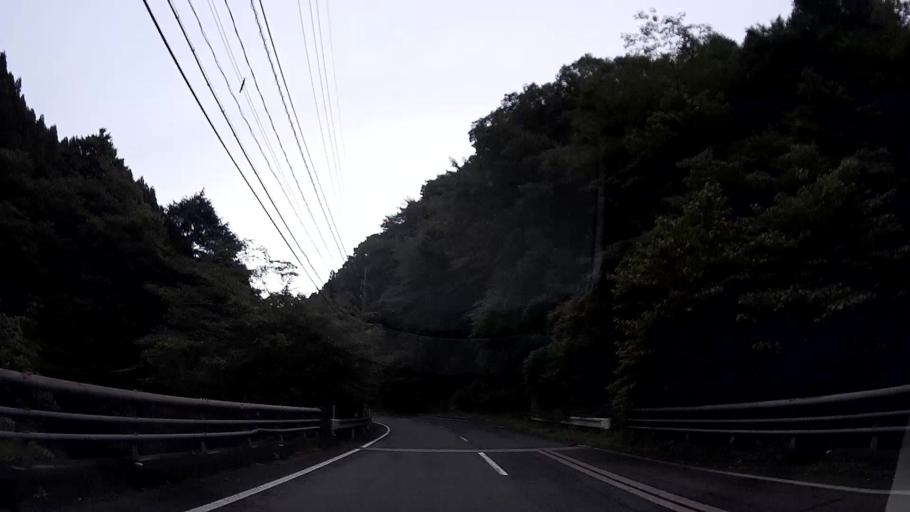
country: JP
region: Kumamoto
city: Kikuchi
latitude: 33.0727
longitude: 130.9237
